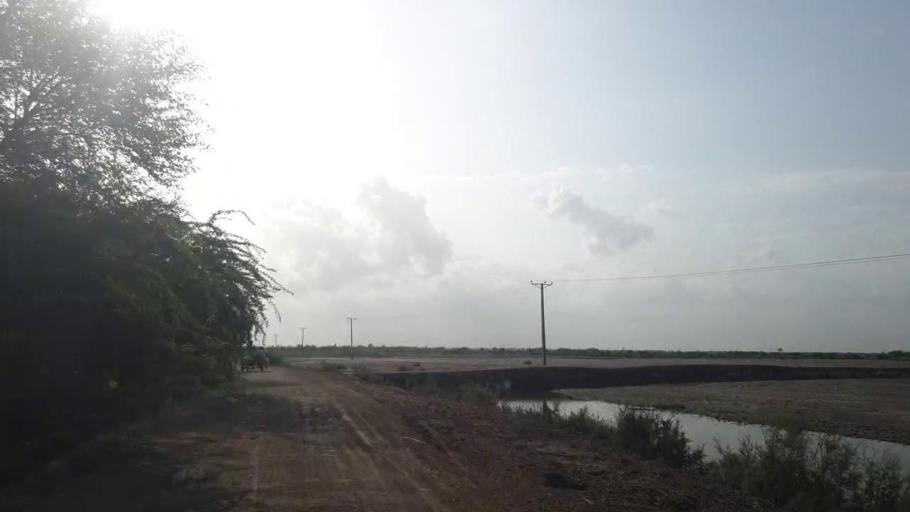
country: PK
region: Sindh
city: Kadhan
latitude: 24.6273
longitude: 69.0893
